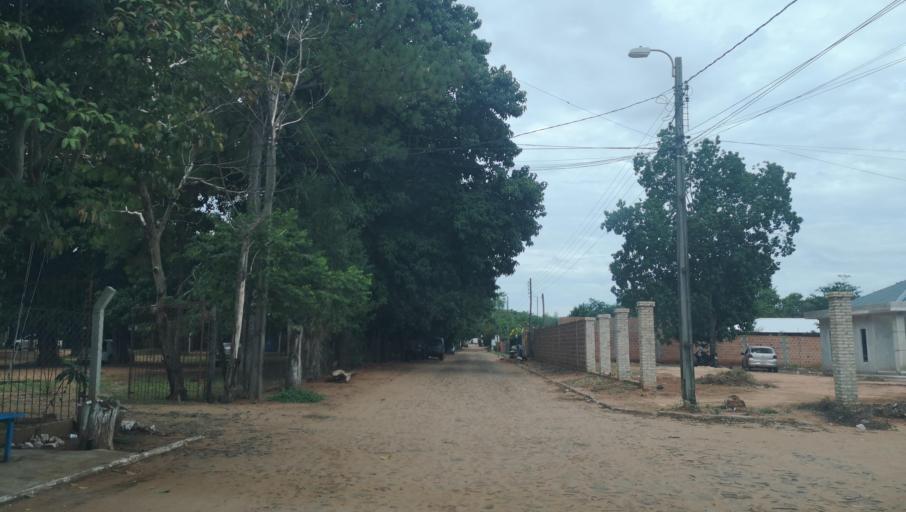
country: PY
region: San Pedro
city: Capiibary
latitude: -24.7274
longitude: -56.0173
